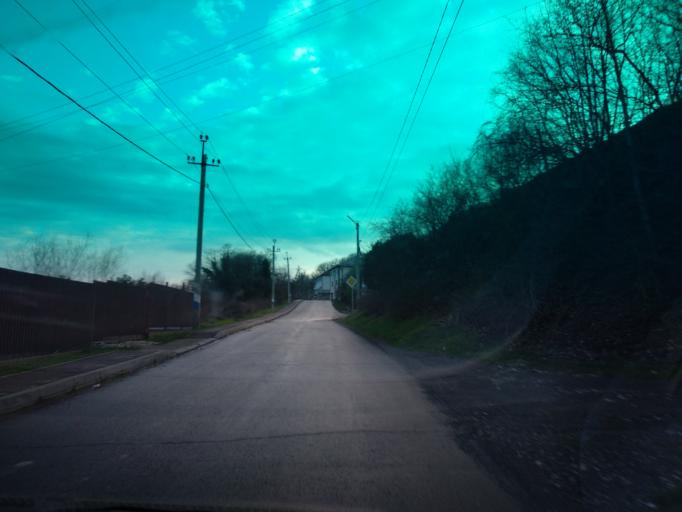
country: RU
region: Krasnodarskiy
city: Novomikhaylovskiy
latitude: 44.2646
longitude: 38.8244
